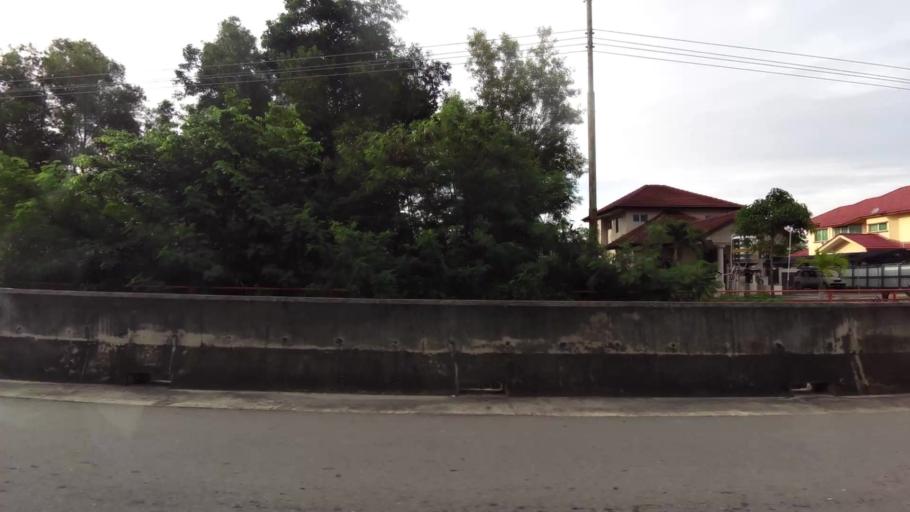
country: BN
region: Brunei and Muara
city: Bandar Seri Begawan
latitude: 4.9053
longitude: 114.8954
